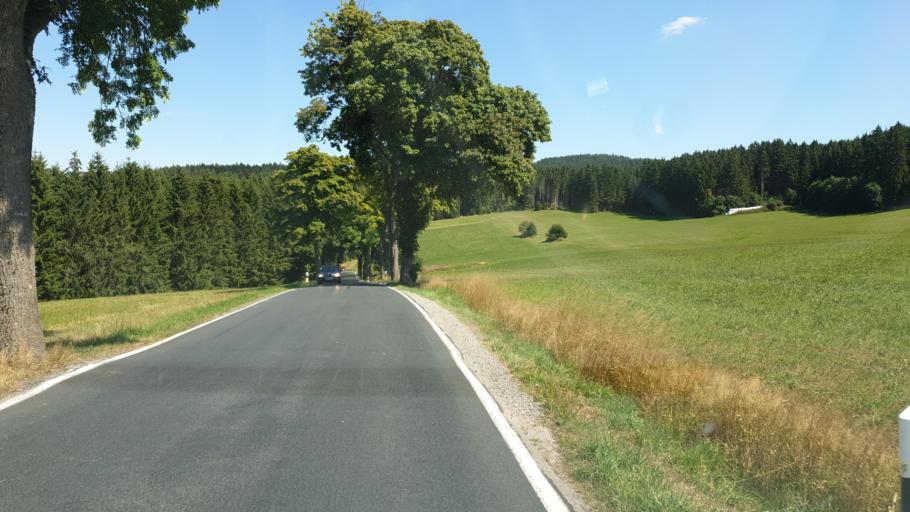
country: DE
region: Saxony
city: Sosa
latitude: 50.5003
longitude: 12.6630
